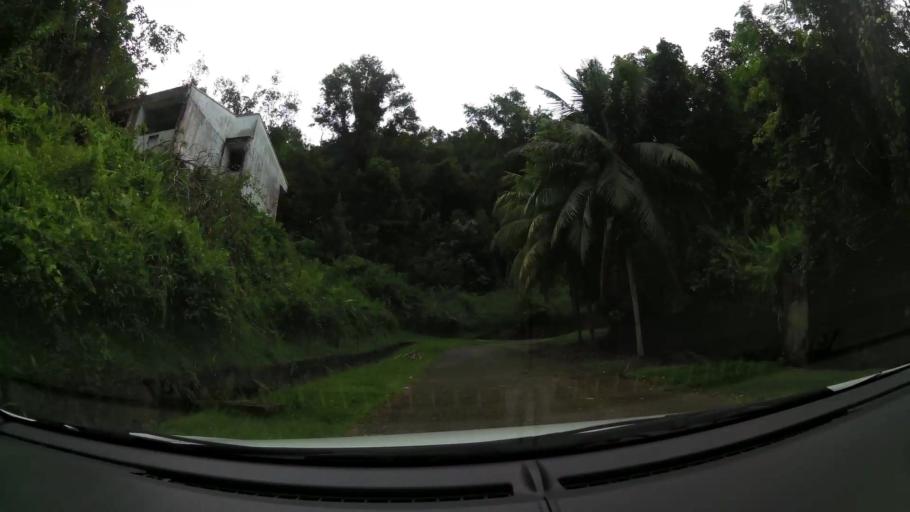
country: BN
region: Brunei and Muara
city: Bandar Seri Begawan
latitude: 4.9088
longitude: 114.9966
